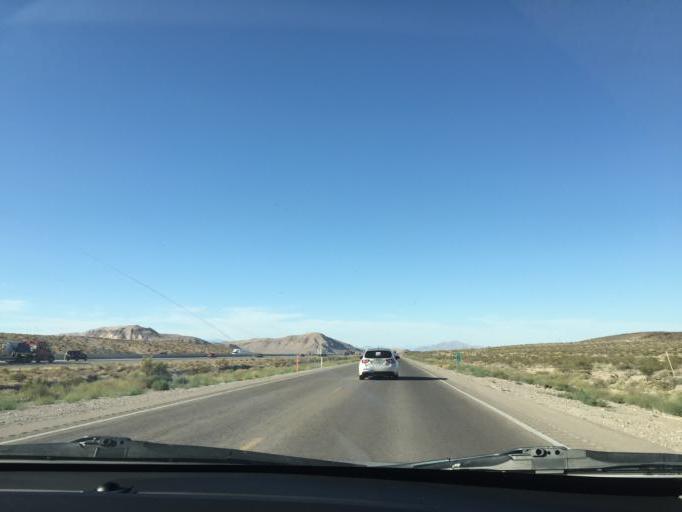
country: US
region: Nevada
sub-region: Clark County
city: Enterprise
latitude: 35.9032
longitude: -115.2113
